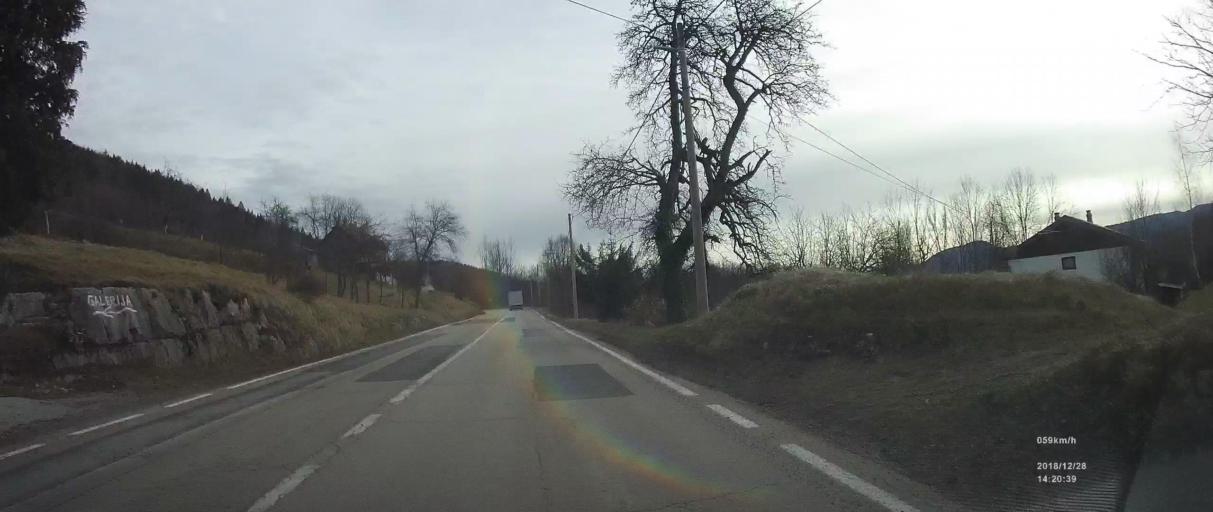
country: HR
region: Primorsko-Goranska
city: Vrbovsko
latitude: 45.3997
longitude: 15.0773
